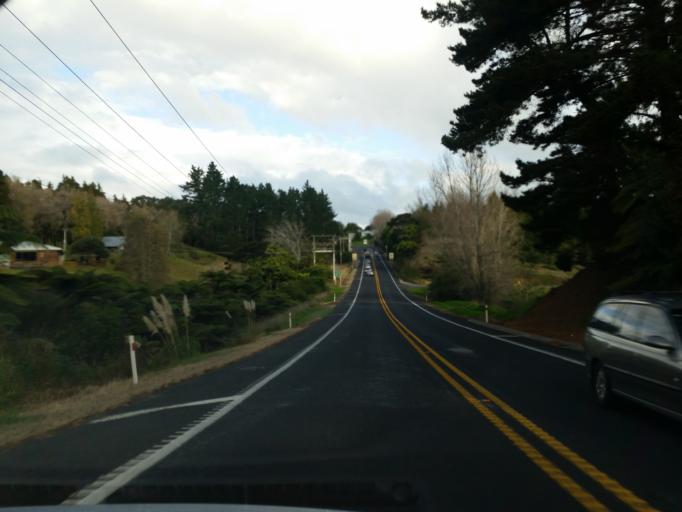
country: NZ
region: Bay of Plenty
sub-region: Western Bay of Plenty District
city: Katikati
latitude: -37.6495
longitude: 175.9949
